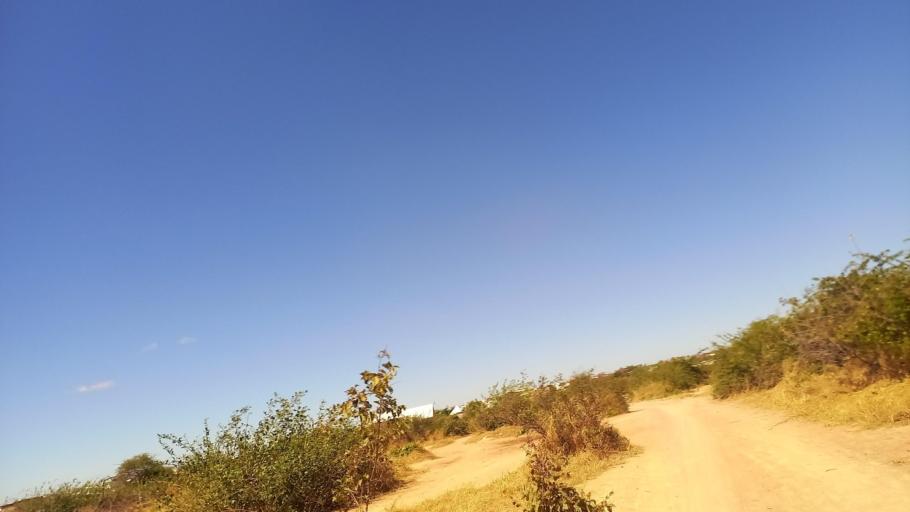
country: TZ
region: Dodoma
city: Dodoma
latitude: -6.1231
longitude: 35.6976
